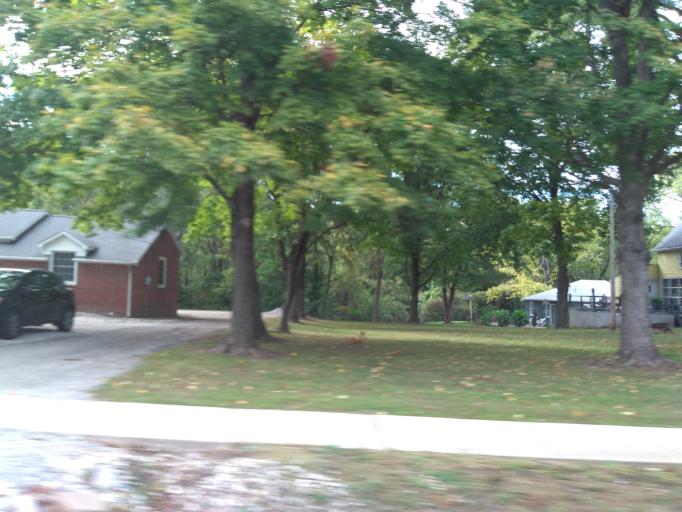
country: US
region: Illinois
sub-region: Bond County
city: Greenville
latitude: 38.8994
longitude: -89.4030
